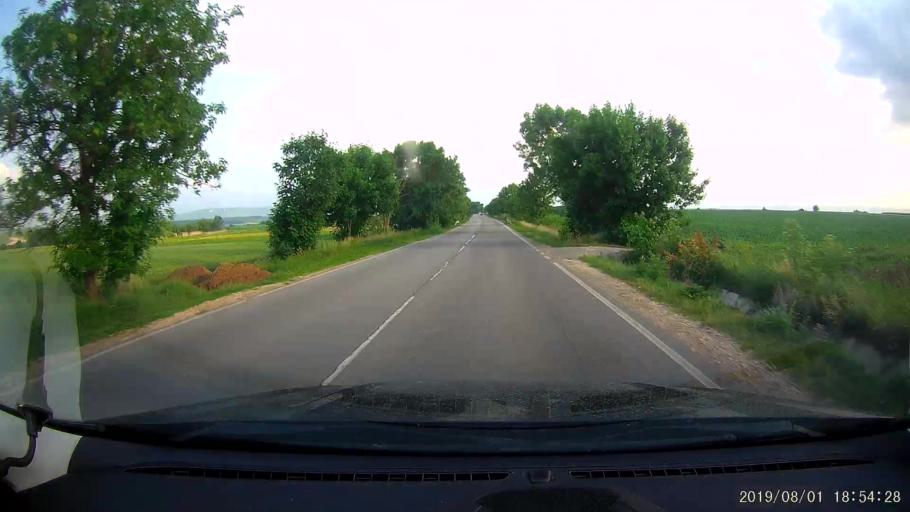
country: BG
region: Shumen
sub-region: Obshtina Shumen
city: Shumen
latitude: 43.1979
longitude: 27.0019
